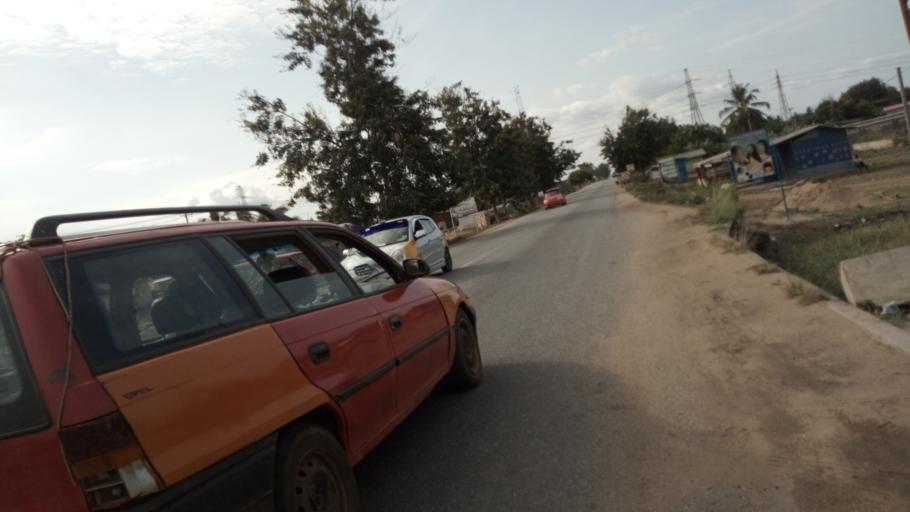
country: GH
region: Central
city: Winneba
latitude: 5.3867
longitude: -0.6442
